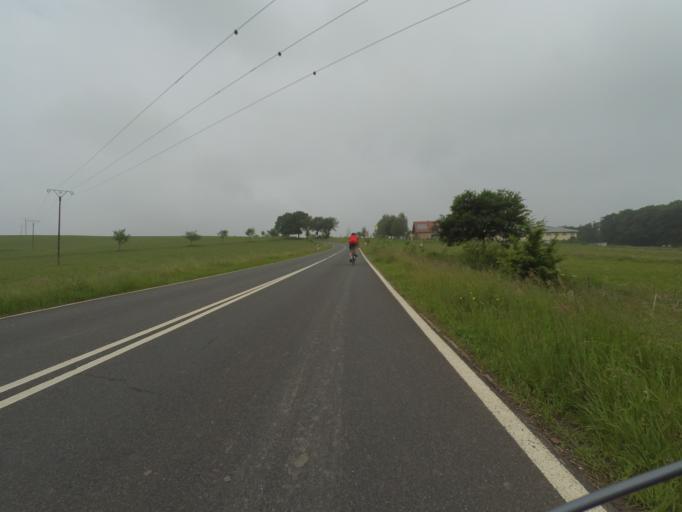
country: DE
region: Rheinland-Pfalz
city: Ernst
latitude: 50.1489
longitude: 7.2582
